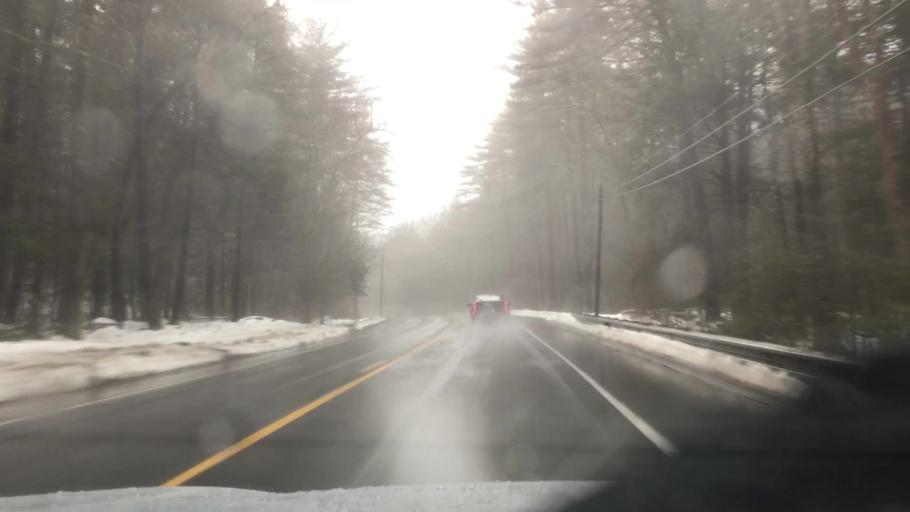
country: US
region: Massachusetts
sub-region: Franklin County
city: Orange
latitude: 42.5298
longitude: -72.3195
